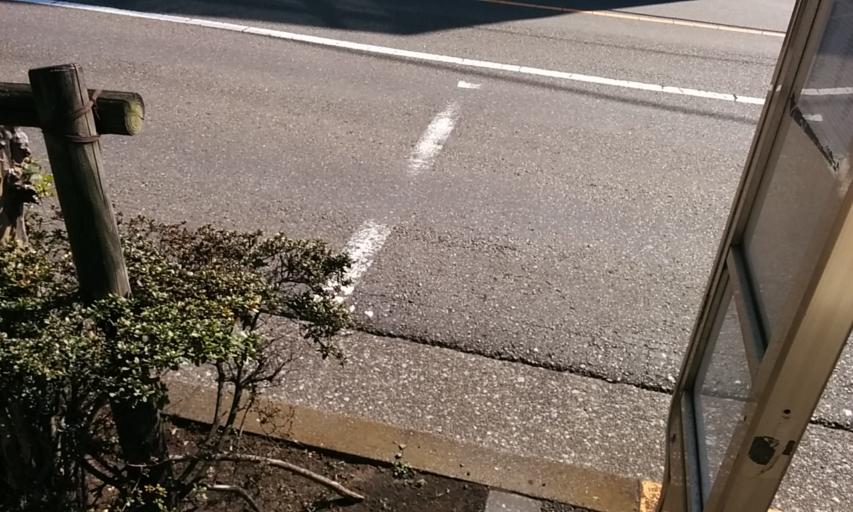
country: JP
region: Tokyo
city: Chofugaoka
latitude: 35.6554
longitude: 139.5745
